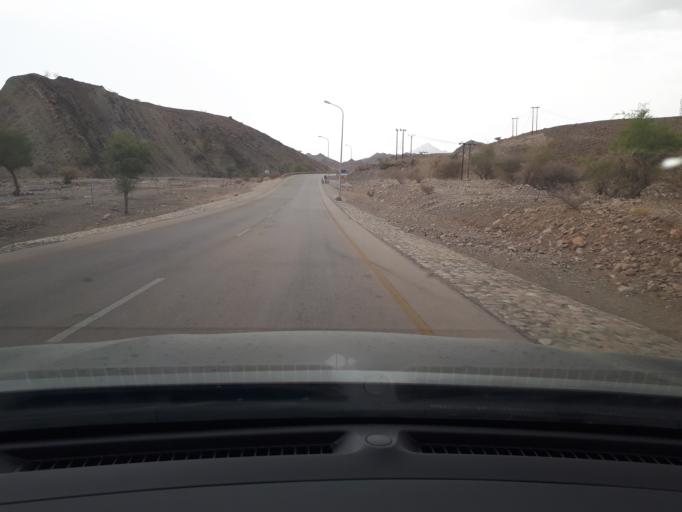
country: OM
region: Ash Sharqiyah
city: Badiyah
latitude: 22.5629
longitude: 59.0366
